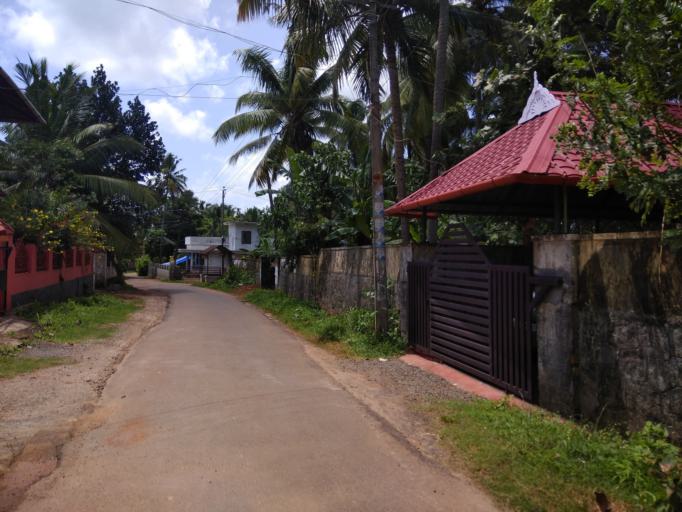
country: IN
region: Kerala
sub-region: Thrissur District
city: Trichur
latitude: 10.5446
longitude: 76.1640
